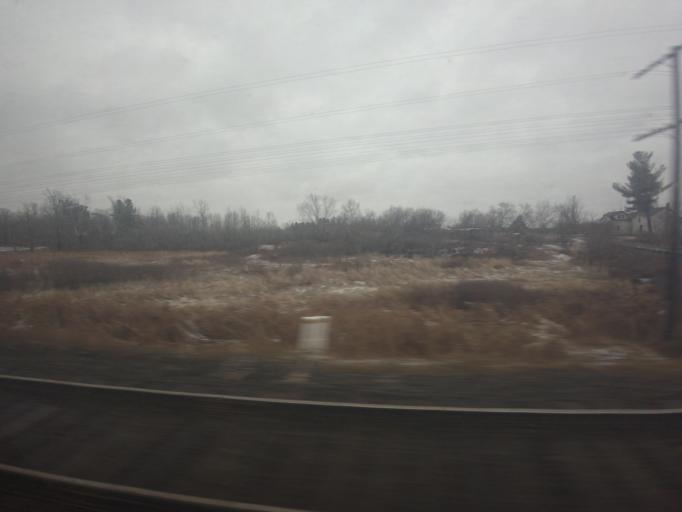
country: CA
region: Ontario
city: Gananoque
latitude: 44.3517
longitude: -76.2502
